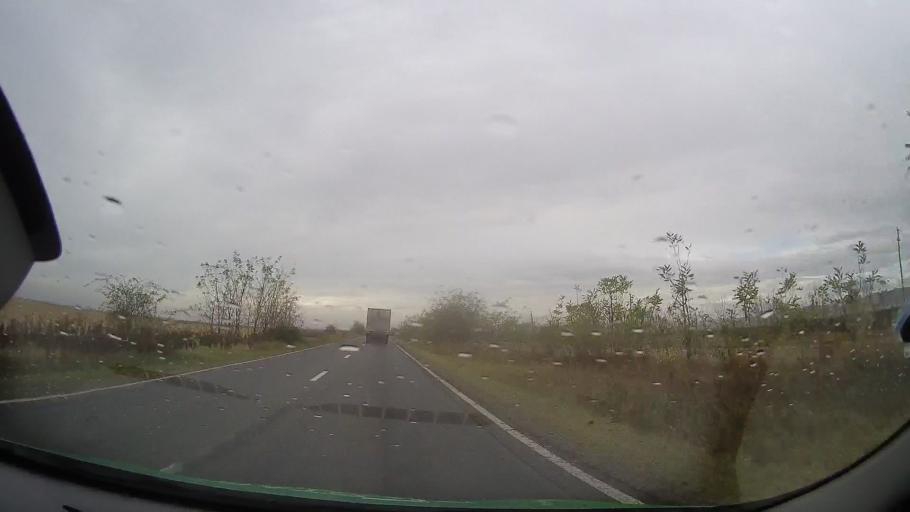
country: RO
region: Prahova
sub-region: Comuna Tomsani
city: Loloiasca
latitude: 44.9753
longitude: 26.3228
